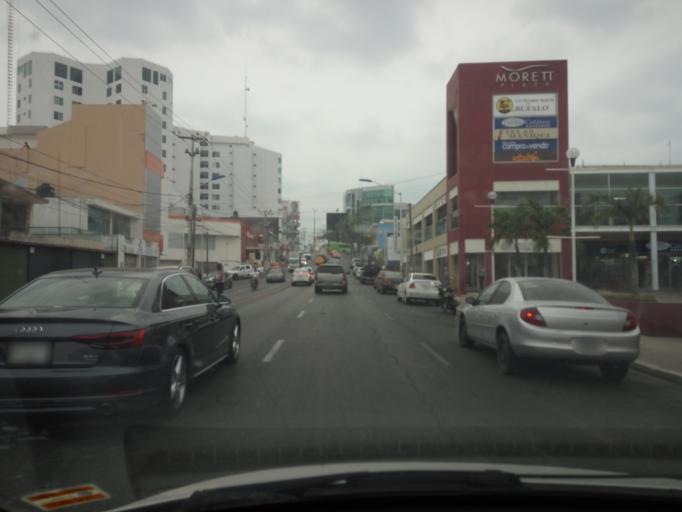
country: MX
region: Tabasco
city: Villahermosa
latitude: 17.9956
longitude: -92.9260
